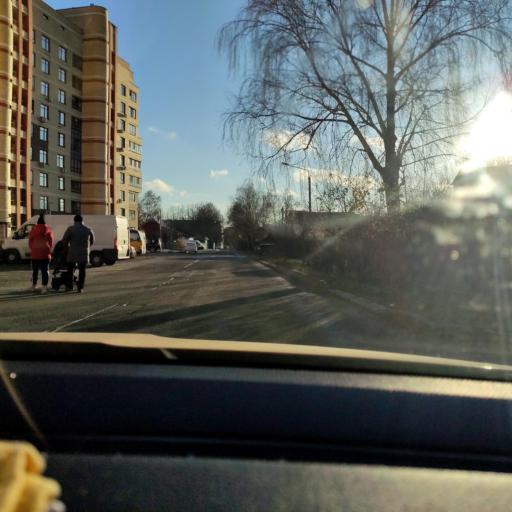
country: RU
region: Moscow
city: Yaroslavskiy
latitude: 55.8946
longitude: 37.7098
